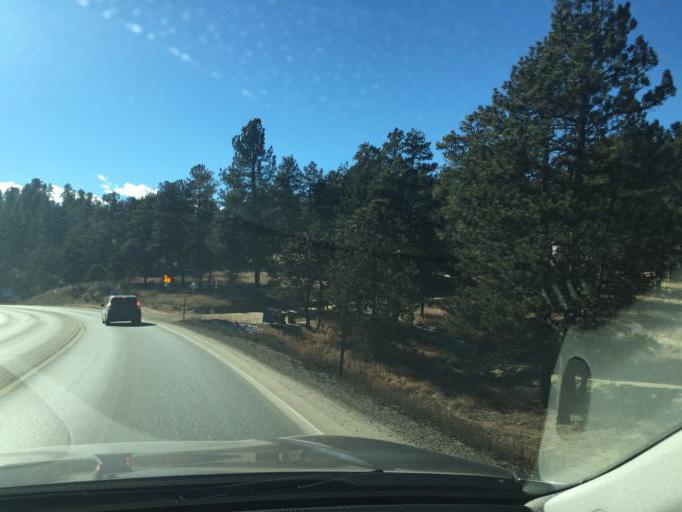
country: US
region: Colorado
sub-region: Jefferson County
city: Evergreen
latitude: 39.4840
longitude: -105.3638
